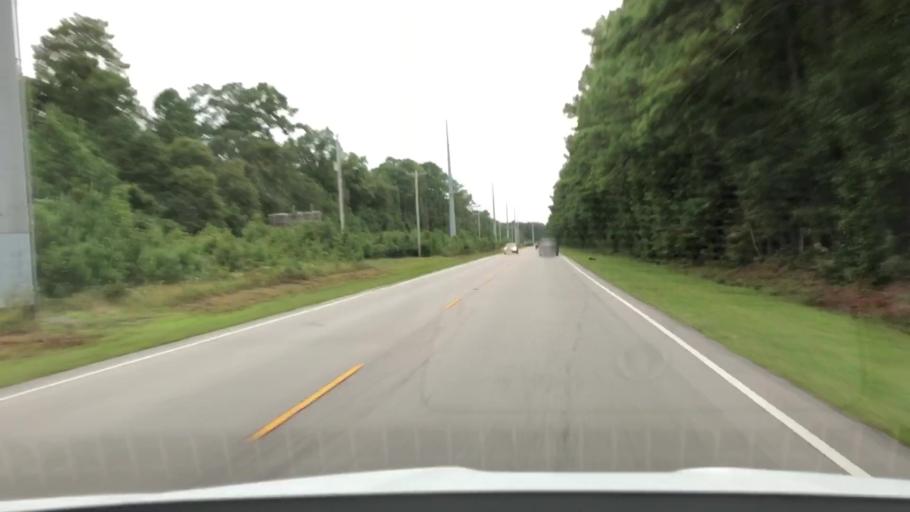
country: US
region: North Carolina
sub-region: Carteret County
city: Cape Carteret
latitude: 34.7424
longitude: -77.0872
